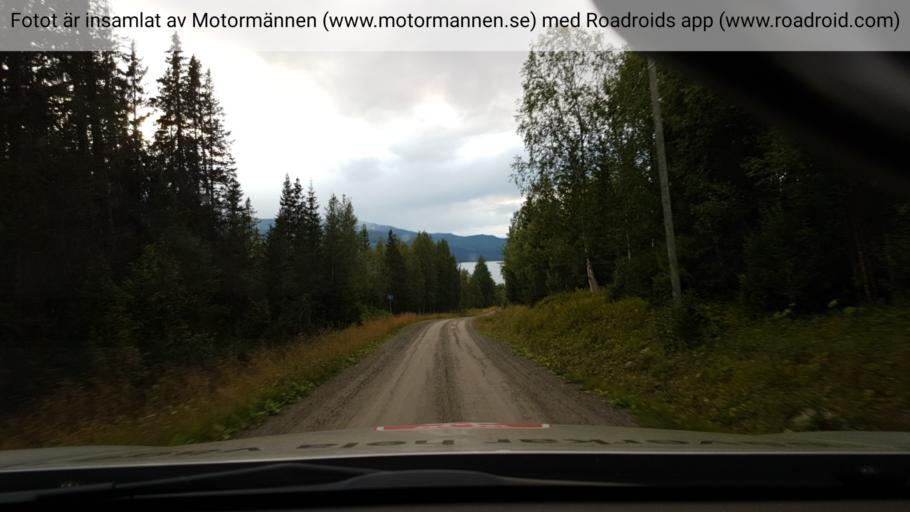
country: SE
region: Vaesterbotten
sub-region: Vilhelmina Kommun
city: Sjoberg
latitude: 65.6128
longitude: 15.2622
